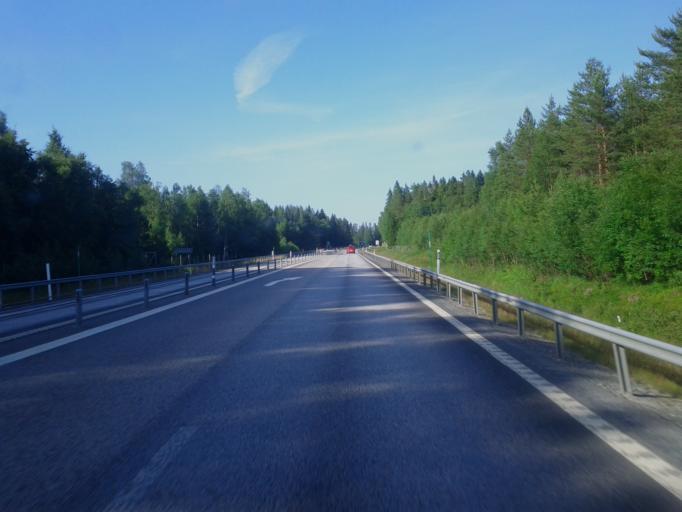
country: SE
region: Vaesterbotten
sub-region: Umea Kommun
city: Saevar
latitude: 63.9136
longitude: 20.5939
